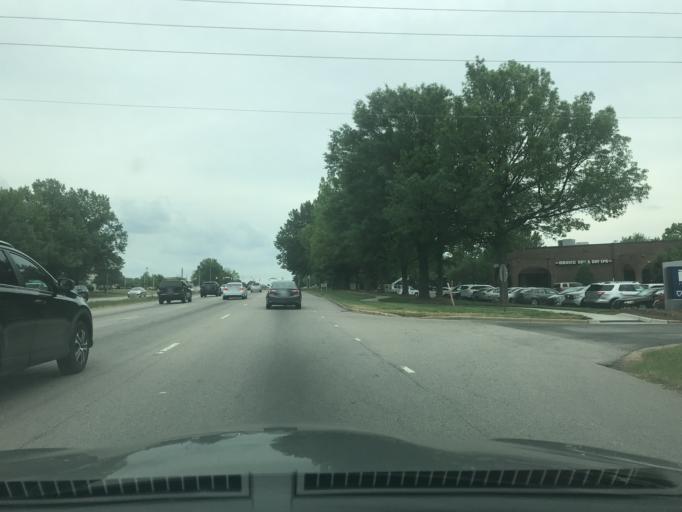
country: US
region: North Carolina
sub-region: Wake County
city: Raleigh
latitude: 35.8578
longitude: -78.5815
